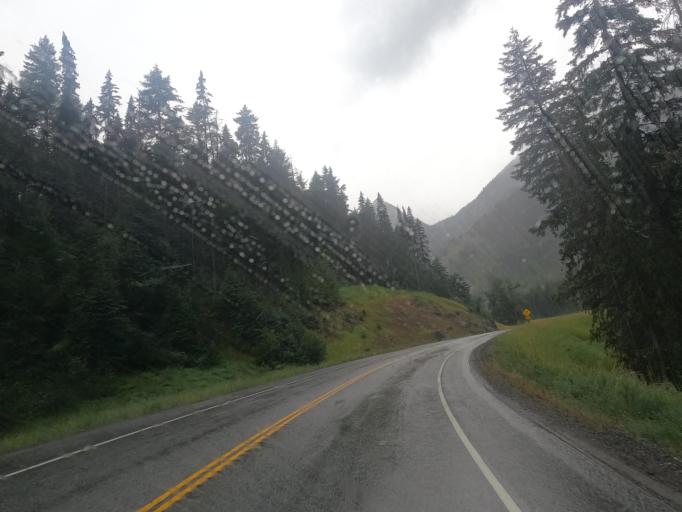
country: CA
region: British Columbia
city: Lillooet
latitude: 50.5336
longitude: -122.1479
